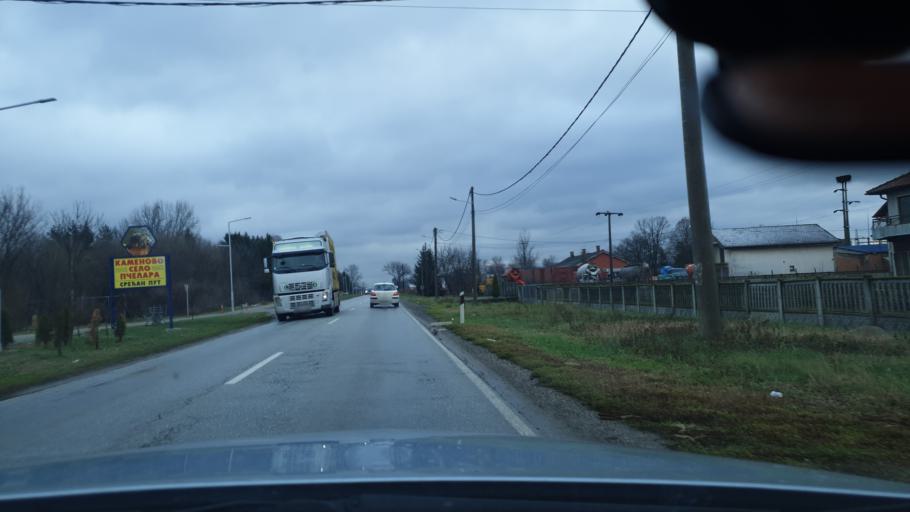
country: RS
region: Central Serbia
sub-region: Branicevski Okrug
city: Petrovac
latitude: 44.3977
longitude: 21.4030
